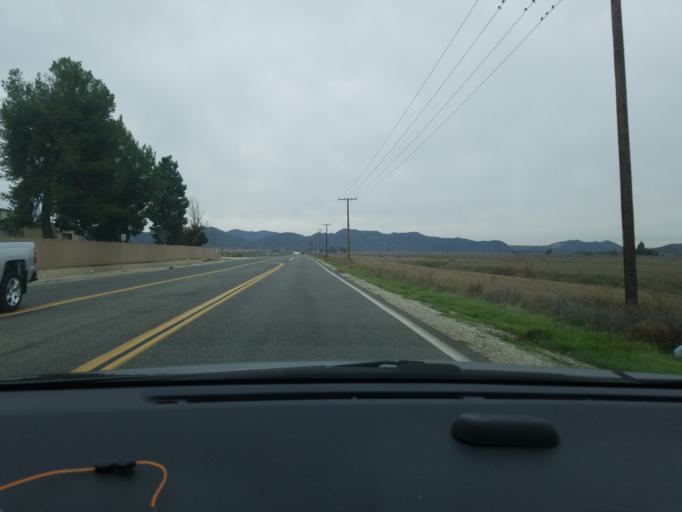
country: US
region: California
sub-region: Riverside County
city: Green Acres
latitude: 33.7359
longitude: -117.0328
